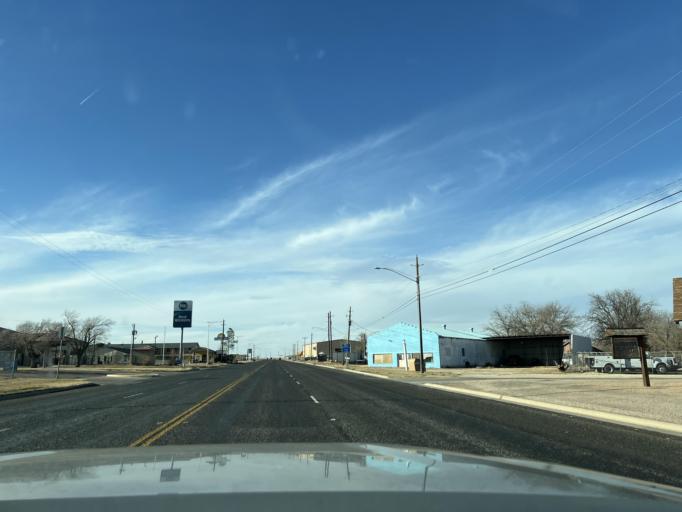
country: US
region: Texas
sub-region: Scurry County
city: Snyder
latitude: 32.7075
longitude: -100.8866
